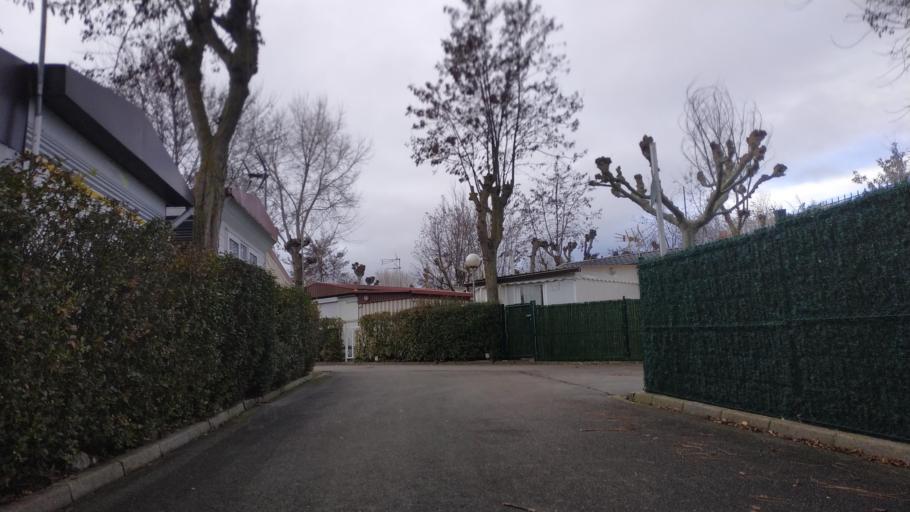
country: ES
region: La Rioja
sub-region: Provincia de La Rioja
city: Banares
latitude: 42.4441
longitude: -2.9172
